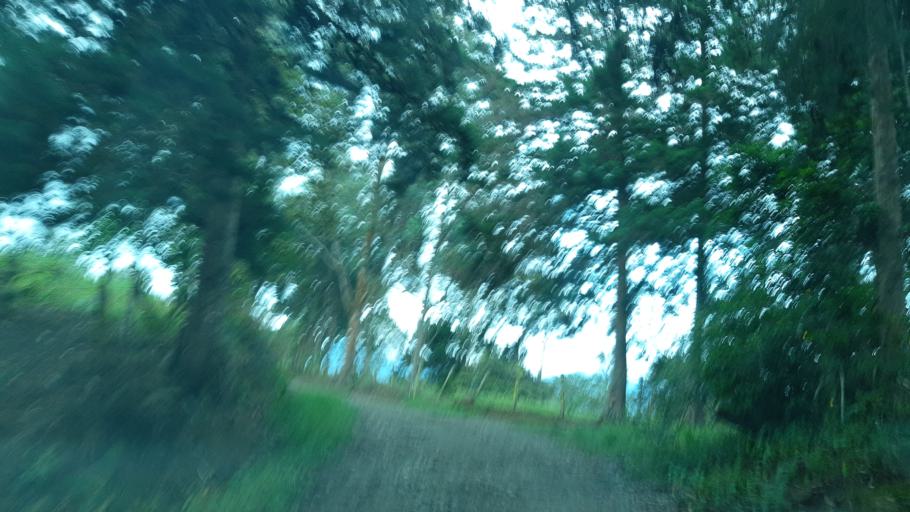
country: CO
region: Boyaca
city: Chinavita
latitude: 5.1356
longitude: -73.3461
